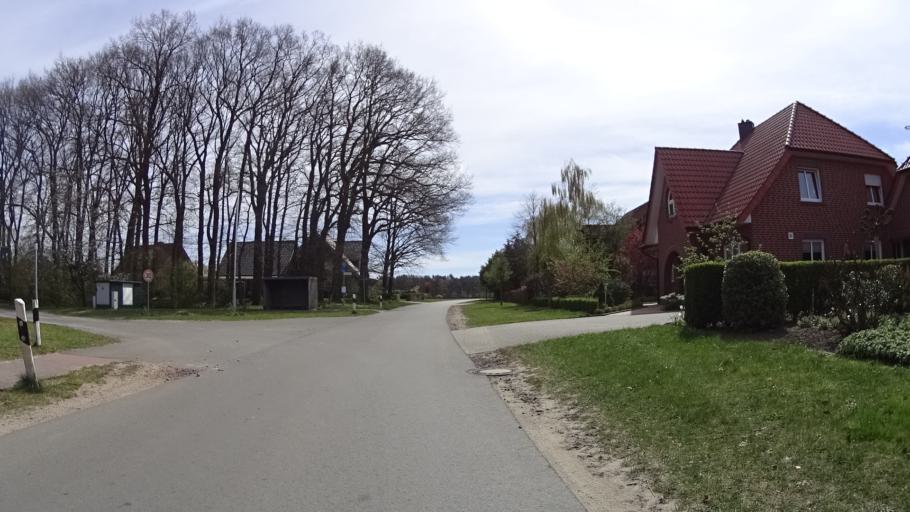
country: DE
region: Lower Saxony
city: Emsburen
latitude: 52.4456
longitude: 7.3417
